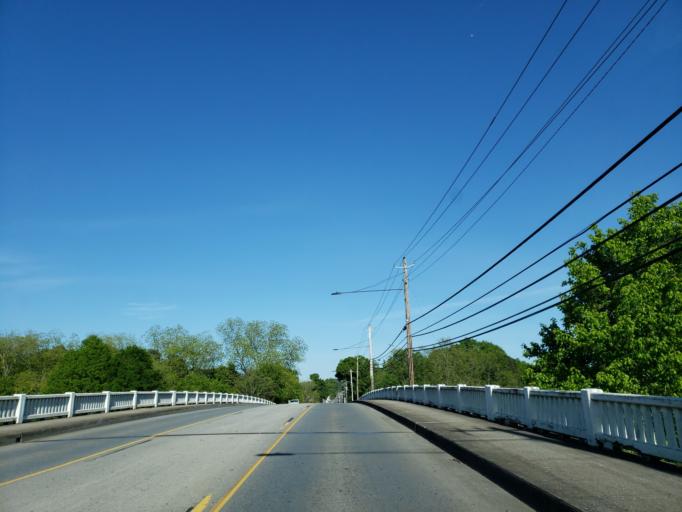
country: US
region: Georgia
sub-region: Polk County
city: Cedartown
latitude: 34.0143
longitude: -85.2491
